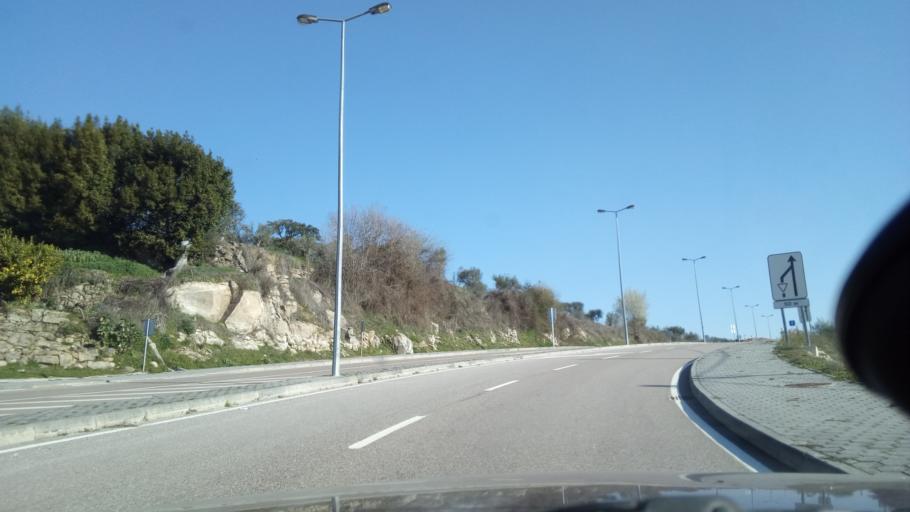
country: PT
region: Guarda
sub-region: Fornos de Algodres
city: Fornos de Algodres
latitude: 40.6159
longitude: -7.5384
